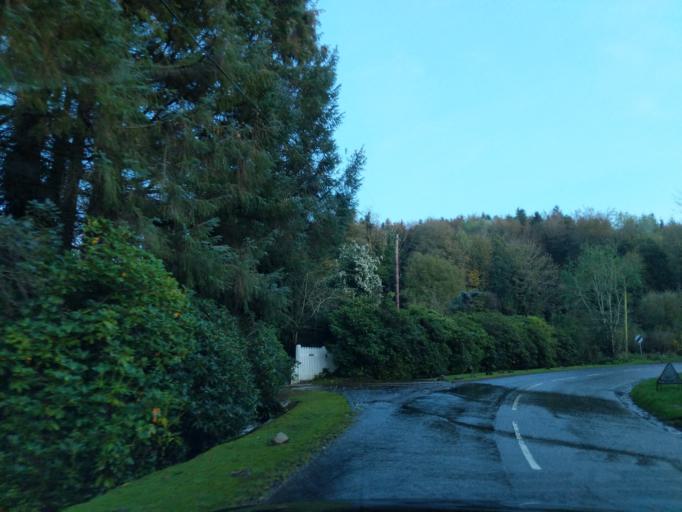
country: GB
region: Scotland
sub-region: Dumfries and Galloway
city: Kirkcudbright
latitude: 54.8371
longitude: -4.0411
